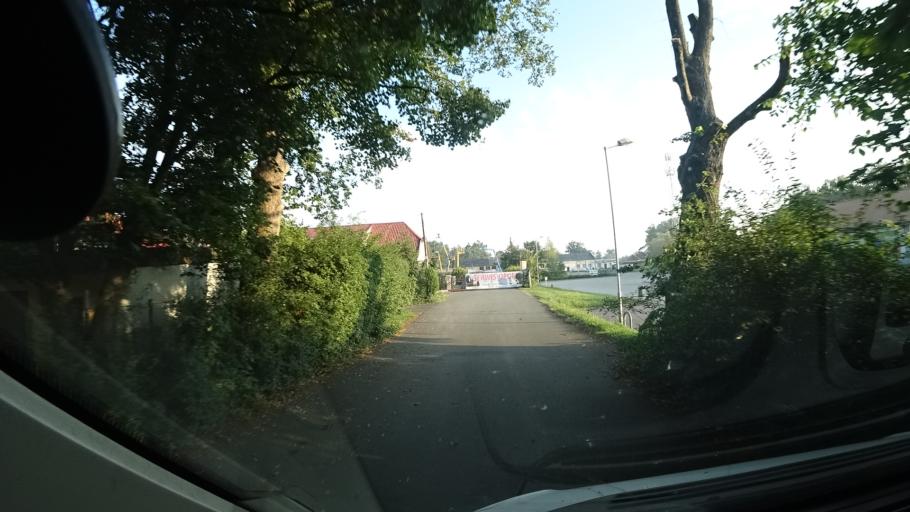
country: PL
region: Opole Voivodeship
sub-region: Powiat kedzierzynsko-kozielski
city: Kedzierzyn-Kozle
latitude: 50.3526
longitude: 18.2349
